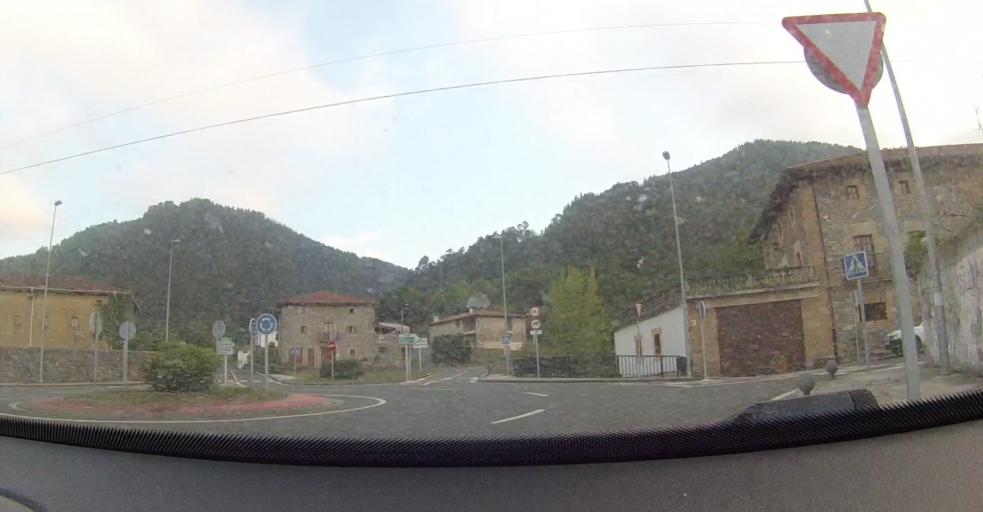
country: ES
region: Basque Country
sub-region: Bizkaia
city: Sopuerta
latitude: 43.2494
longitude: -3.1555
